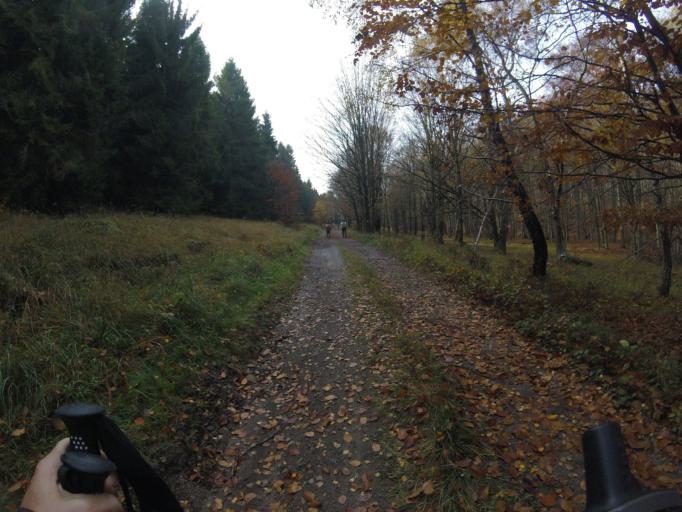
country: HU
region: Borsod-Abauj-Zemplen
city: Gonc
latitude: 48.4291
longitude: 21.3738
